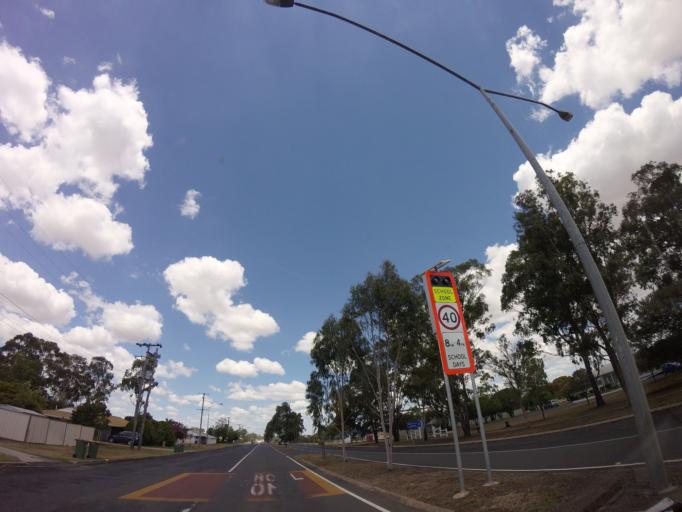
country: AU
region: Queensland
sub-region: Toowoomba
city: Oakey
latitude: -27.8781
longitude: 151.2630
